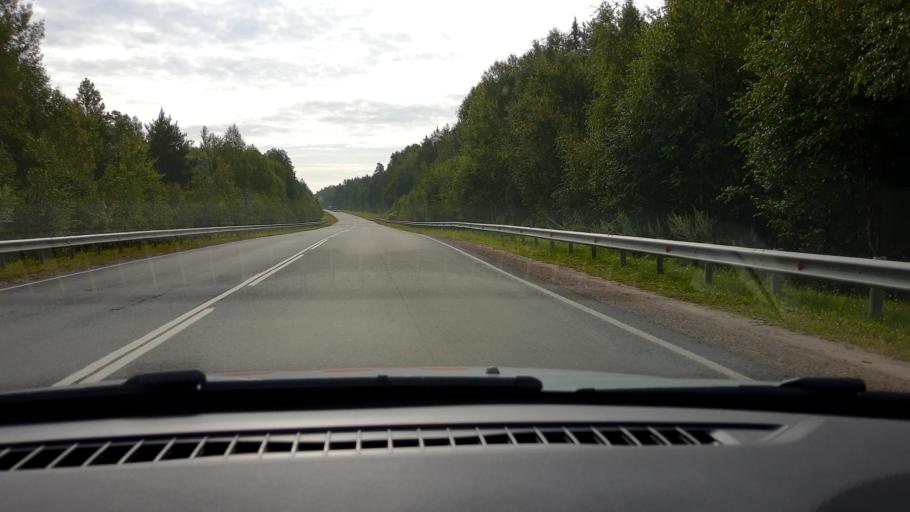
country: RU
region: Nizjnij Novgorod
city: Semenov
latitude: 56.8210
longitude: 44.5139
